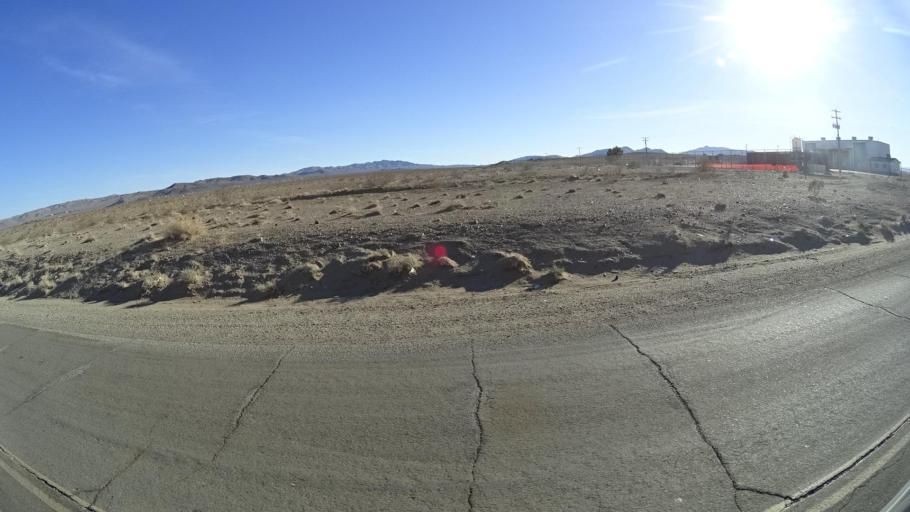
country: US
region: California
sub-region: Kern County
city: China Lake Acres
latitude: 35.6080
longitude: -117.7354
